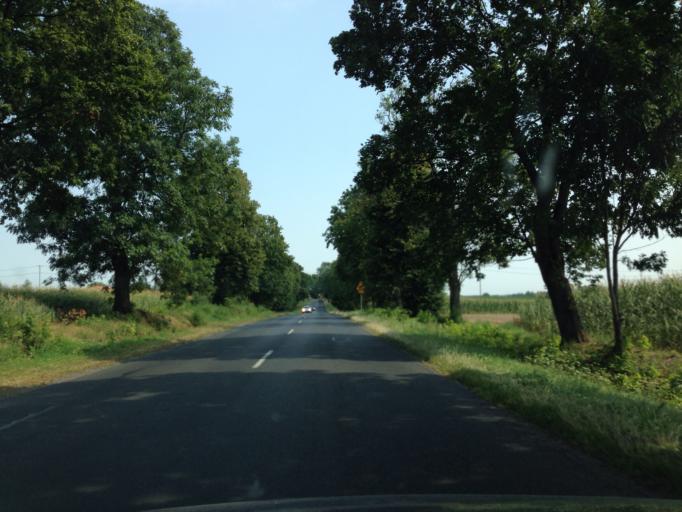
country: PL
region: Kujawsko-Pomorskie
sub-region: Powiat rypinski
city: Rypin
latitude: 53.0681
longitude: 19.3652
